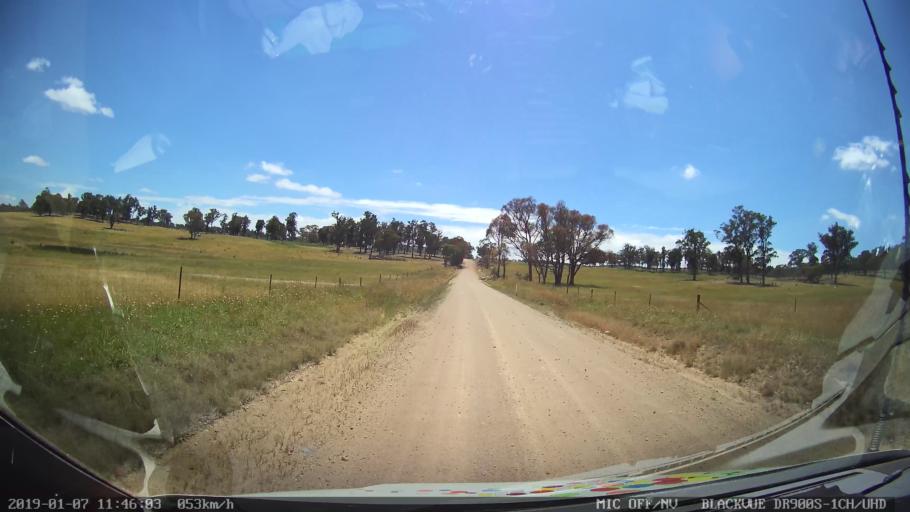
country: AU
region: New South Wales
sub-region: Guyra
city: Guyra
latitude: -30.3443
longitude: 151.6105
